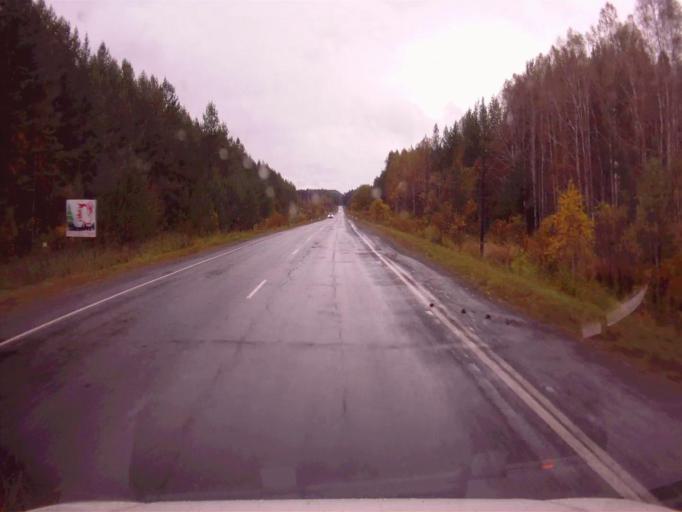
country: RU
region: Chelyabinsk
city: Verkhniy Ufaley
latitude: 56.0138
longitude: 60.3126
